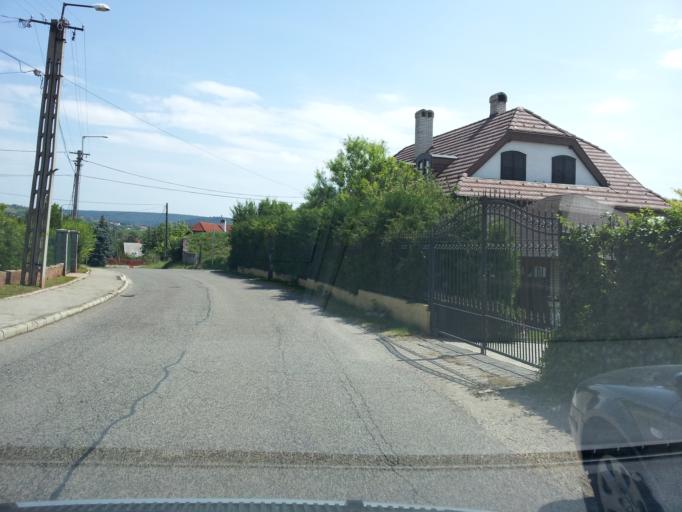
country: HU
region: Veszprem
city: Csopak
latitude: 46.9837
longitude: 17.9419
